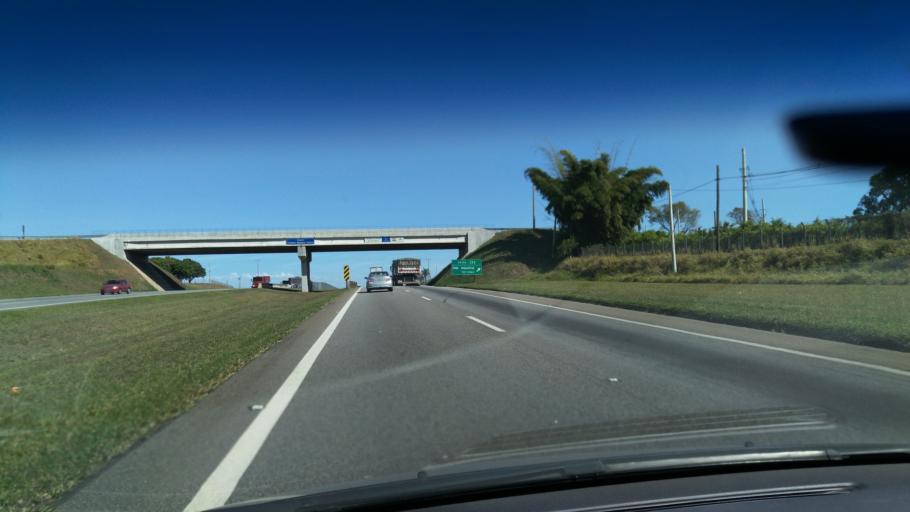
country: BR
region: Sao Paulo
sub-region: Jaguariuna
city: Jaguariuna
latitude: -22.6802
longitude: -47.0066
